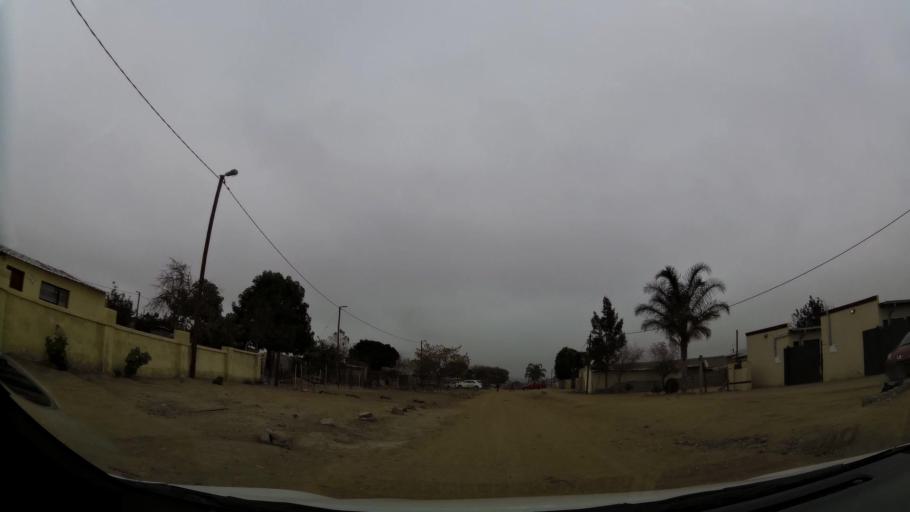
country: ZA
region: Limpopo
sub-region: Capricorn District Municipality
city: Polokwane
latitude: -23.8337
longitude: 29.3913
